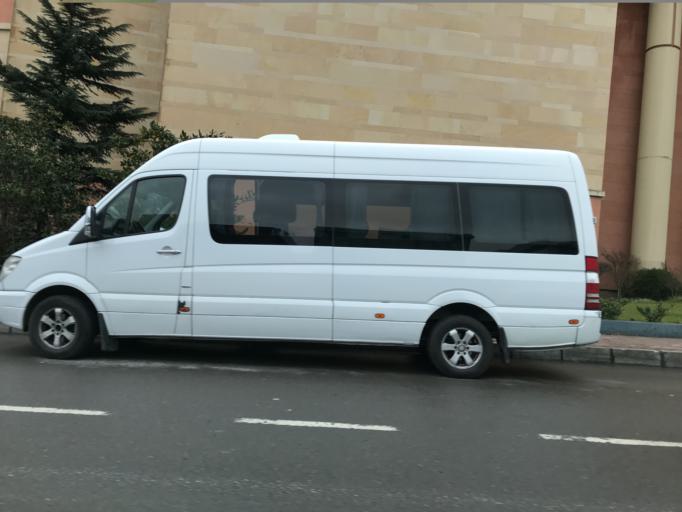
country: TR
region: Istanbul
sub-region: Atasehir
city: Atasehir
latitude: 40.9862
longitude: 29.0993
